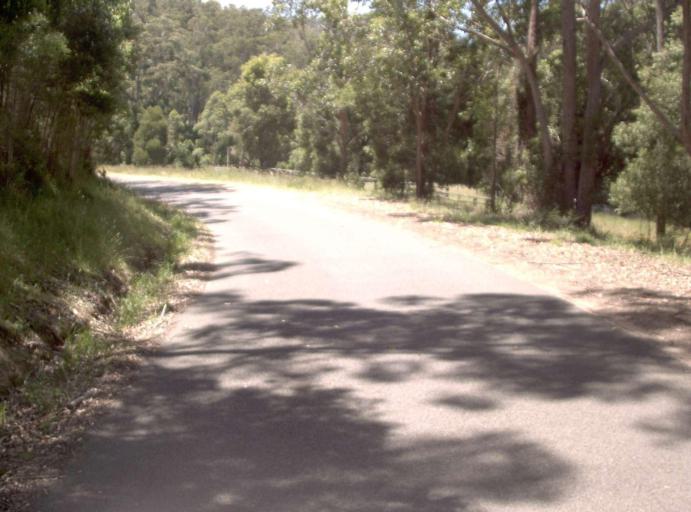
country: AU
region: New South Wales
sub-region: Bombala
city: Bombala
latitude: -37.4636
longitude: 148.9383
